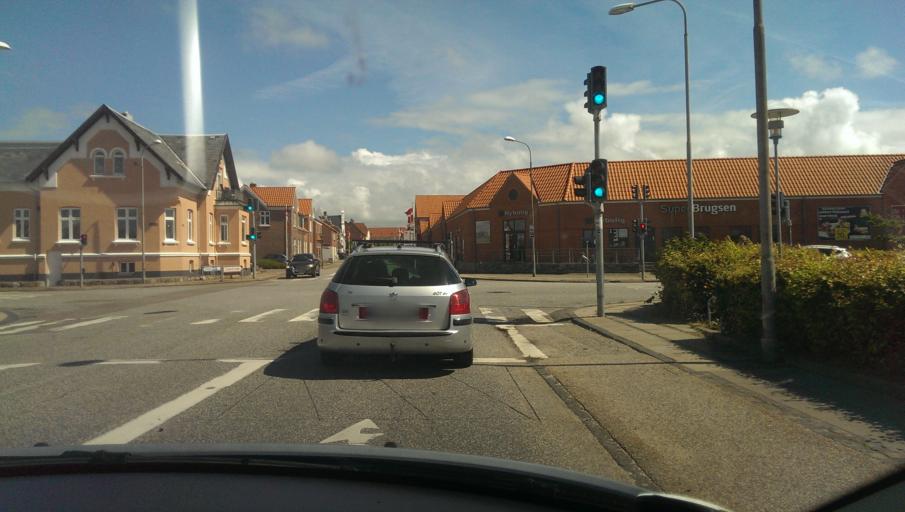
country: DK
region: Central Jutland
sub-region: Ringkobing-Skjern Kommune
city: Ringkobing
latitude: 56.0914
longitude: 8.2399
